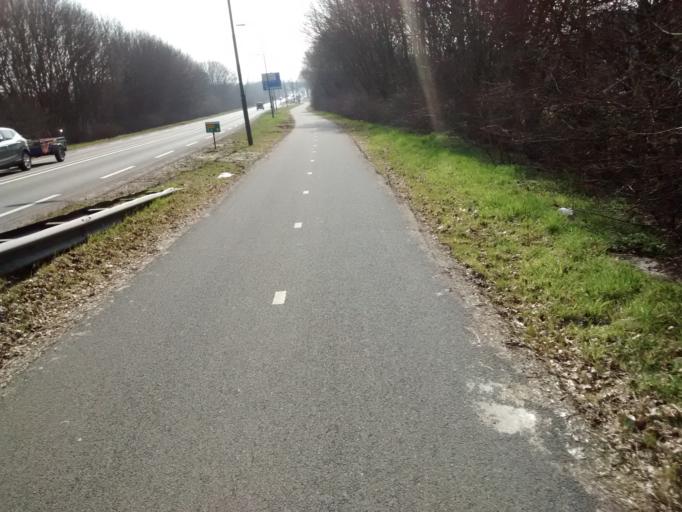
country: NL
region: Utrecht
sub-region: Gemeente Nieuwegein
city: Nieuwegein
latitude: 52.0402
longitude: 5.1045
